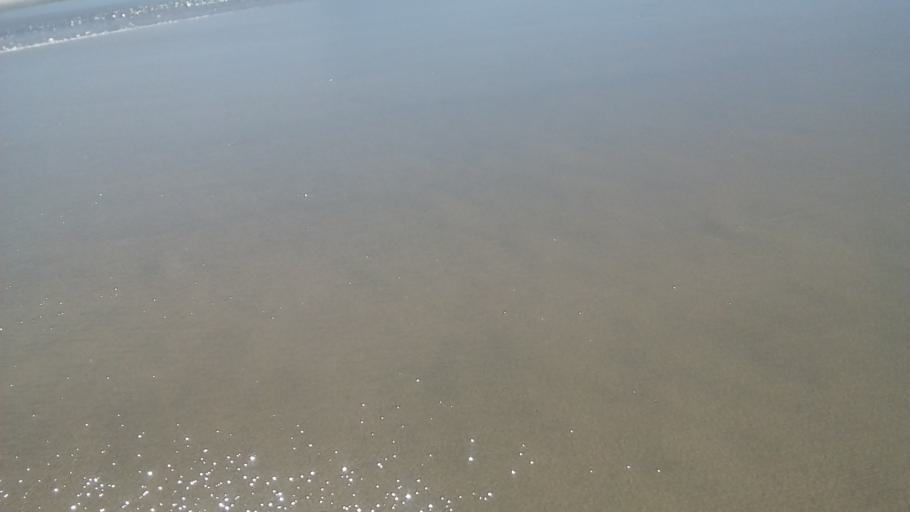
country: CR
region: Guanacaste
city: Santa Cruz
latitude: 10.3266
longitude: -85.8438
